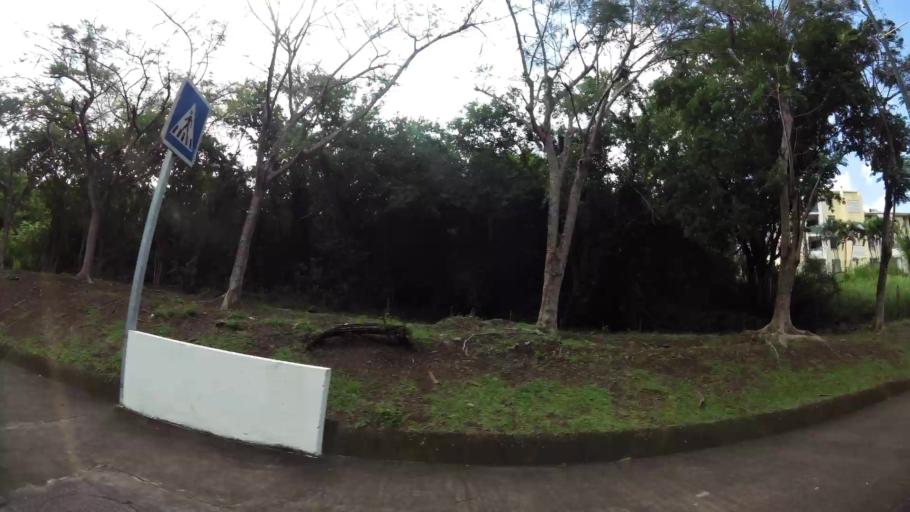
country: MQ
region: Martinique
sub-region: Martinique
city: Les Trois-Ilets
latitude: 14.4807
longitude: -61.0123
